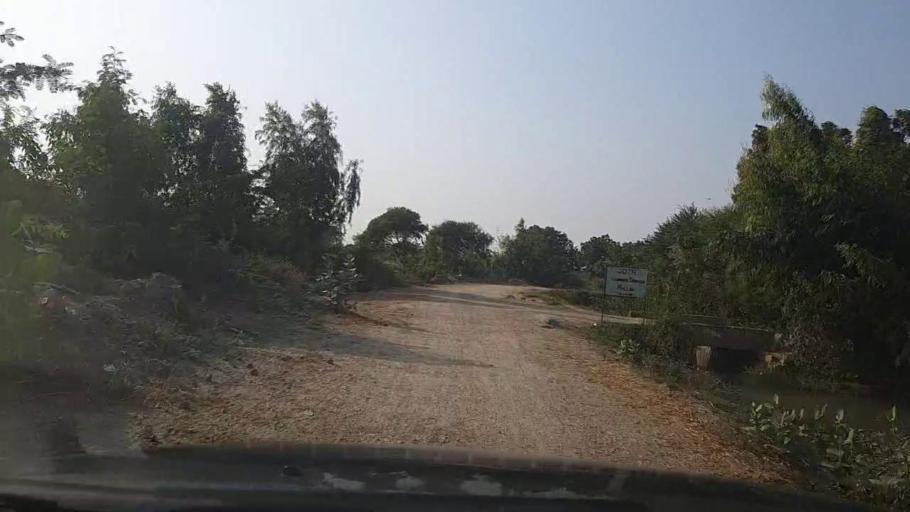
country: PK
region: Sindh
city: Mirpur Sakro
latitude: 24.6391
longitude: 67.7460
